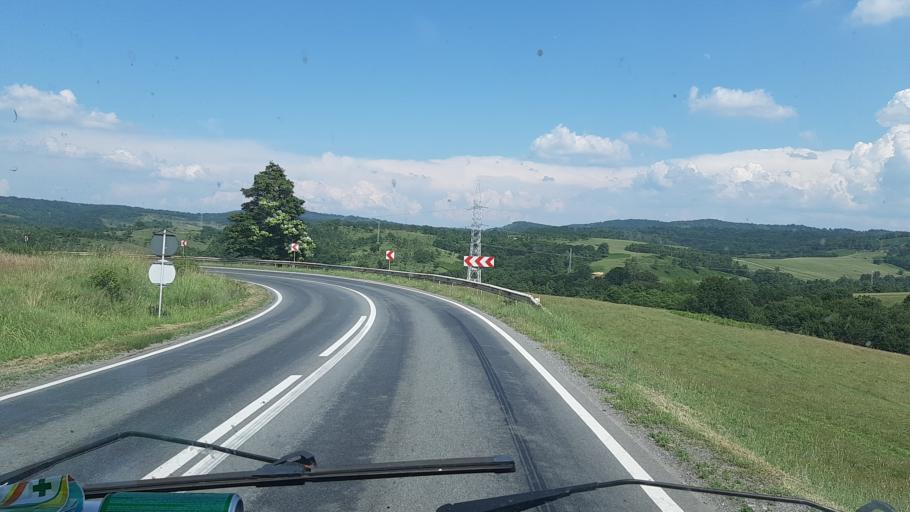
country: RO
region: Caras-Severin
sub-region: Comuna Ezeris
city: Ezeris
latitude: 45.3683
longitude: 21.9298
